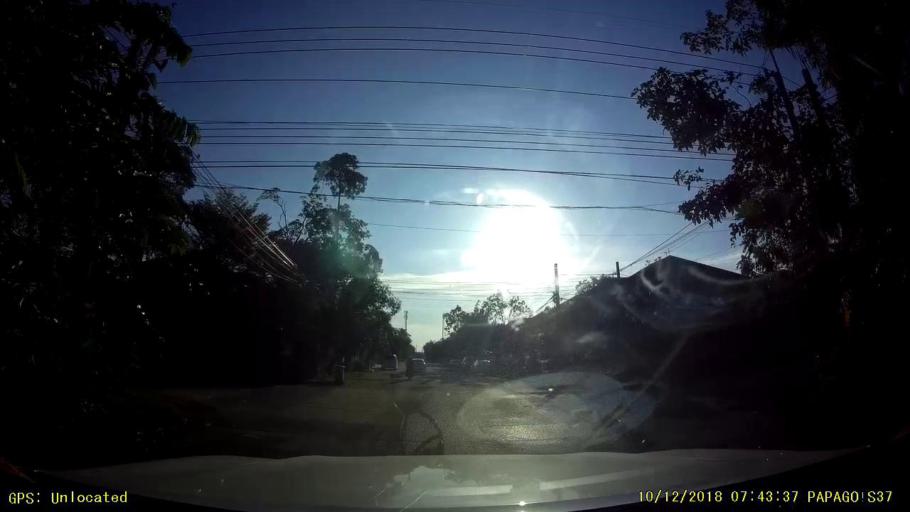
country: TH
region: Bangkok
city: Lat Krabang
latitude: 13.7918
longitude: 100.8144
